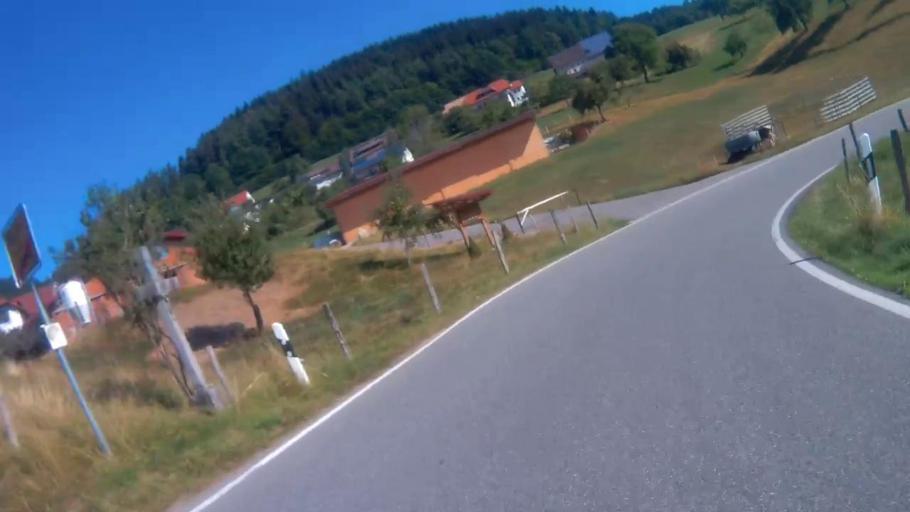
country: DE
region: Baden-Wuerttemberg
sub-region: Freiburg Region
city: Zell im Wiesental
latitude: 47.7171
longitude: 7.8386
